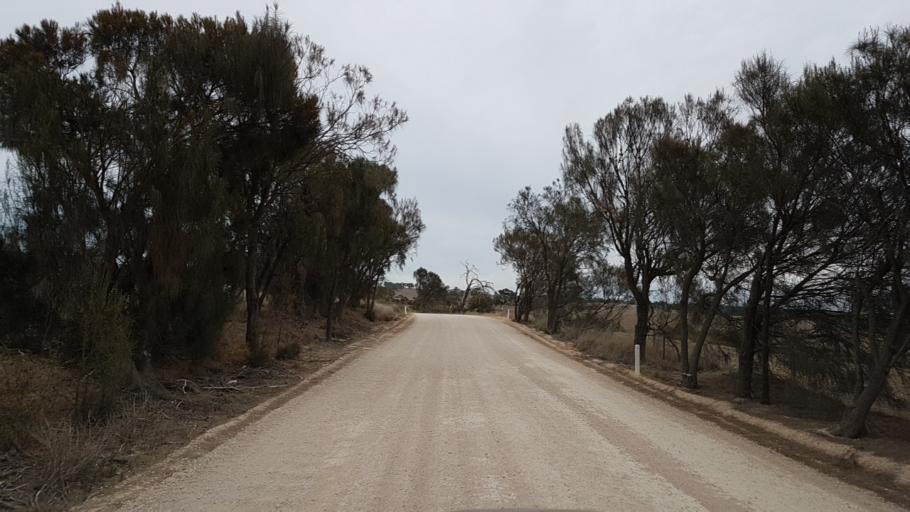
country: AU
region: South Australia
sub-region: Mount Barker
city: Nairne
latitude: -35.0012
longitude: 138.9991
